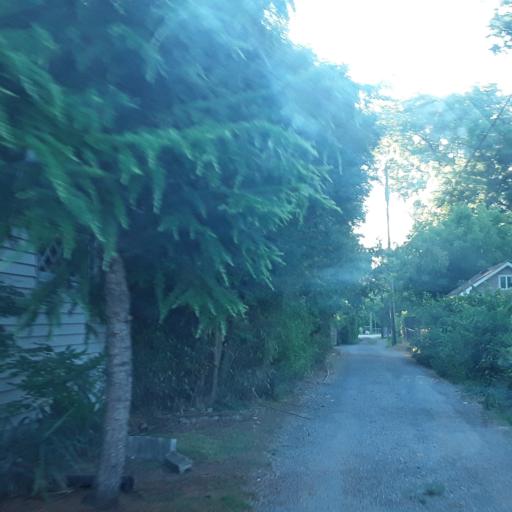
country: US
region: Tennessee
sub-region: Davidson County
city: Oak Hill
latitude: 36.1017
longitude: -86.7335
